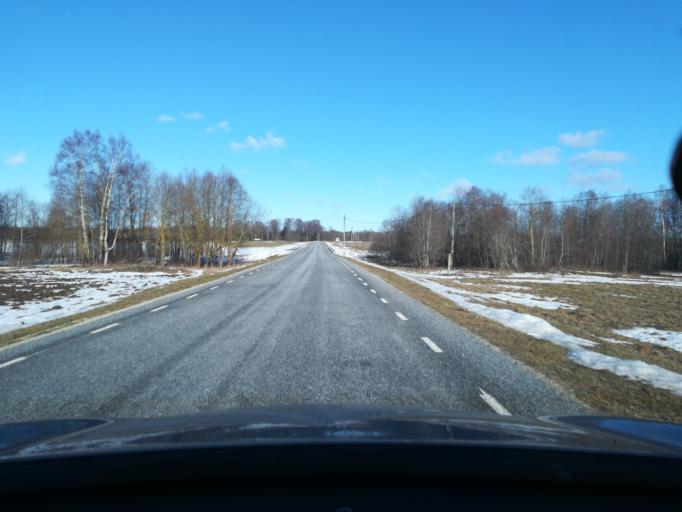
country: EE
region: Harju
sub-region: Kiili vald
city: Kiili
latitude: 59.2643
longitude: 24.8654
